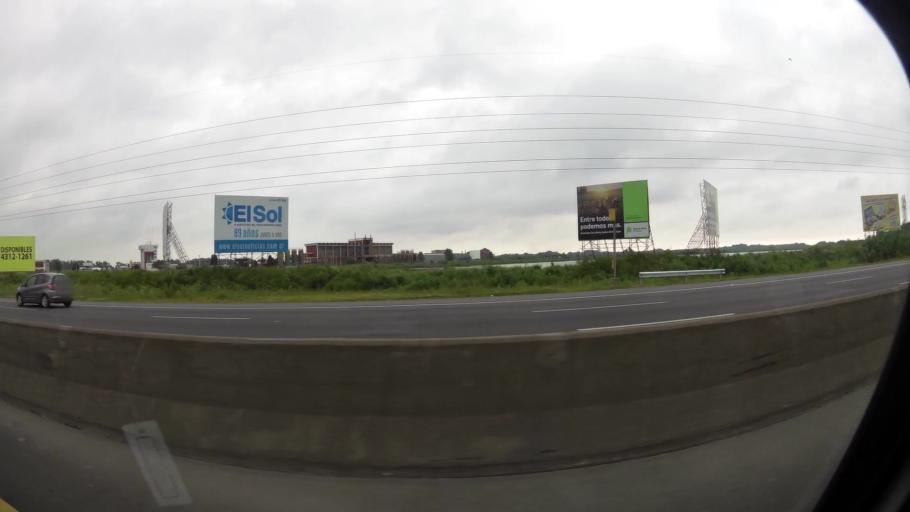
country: AR
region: Buenos Aires
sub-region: Partido de Quilmes
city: Quilmes
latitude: -34.7058
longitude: -58.2658
